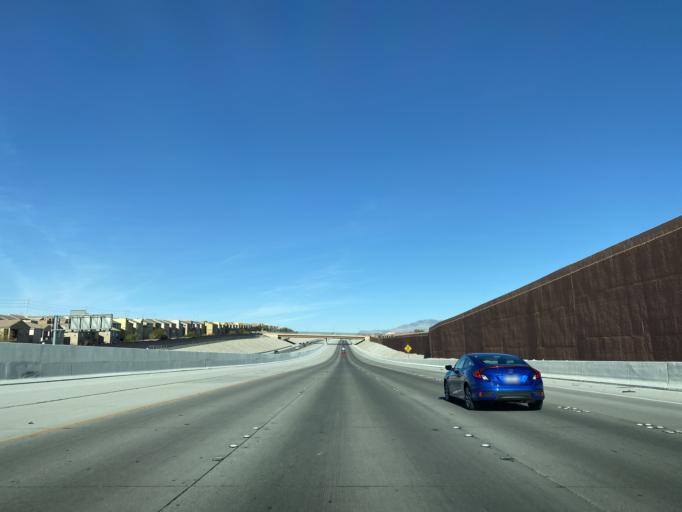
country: US
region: Nevada
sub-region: Clark County
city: Summerlin South
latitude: 36.2280
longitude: -115.3253
